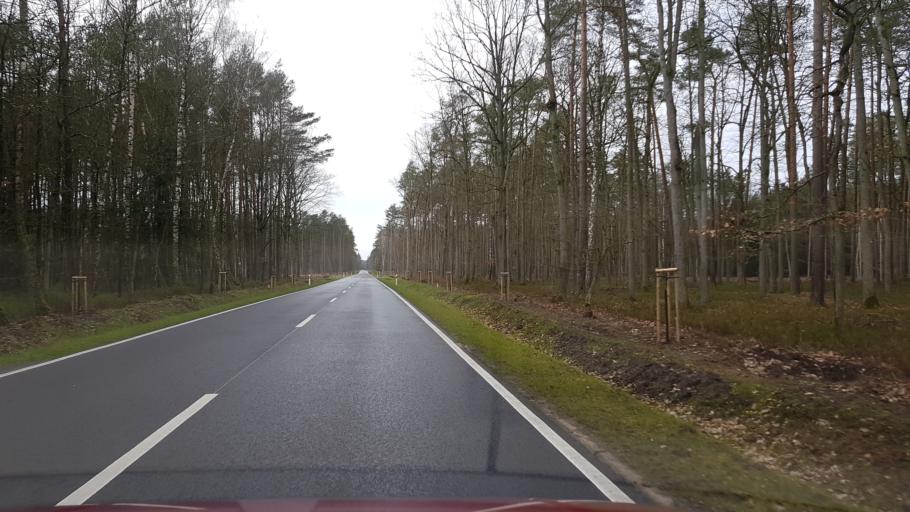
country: PL
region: West Pomeranian Voivodeship
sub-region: Powiat policki
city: Police
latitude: 53.6655
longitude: 14.4478
